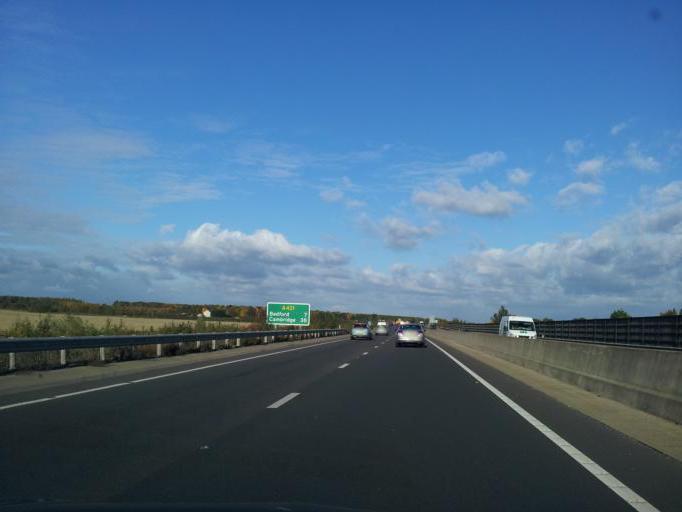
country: GB
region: England
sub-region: Central Bedfordshire
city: Marston Moretaine
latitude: 52.0734
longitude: -0.5404
